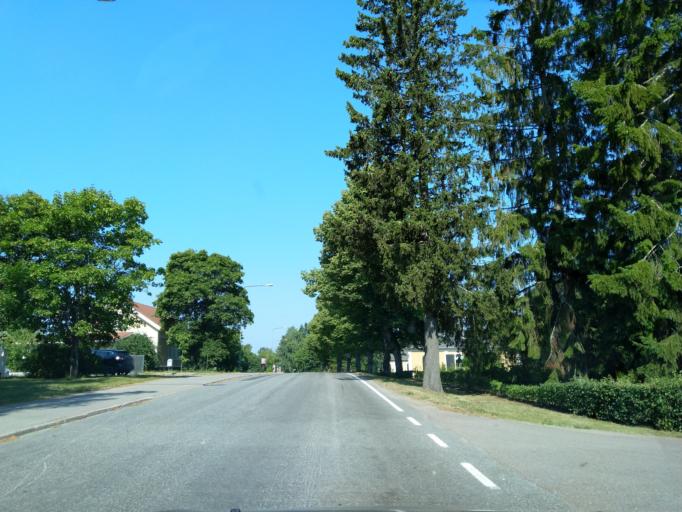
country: FI
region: Satakunta
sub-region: Pori
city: Noormarkku
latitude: 61.5919
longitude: 21.8771
